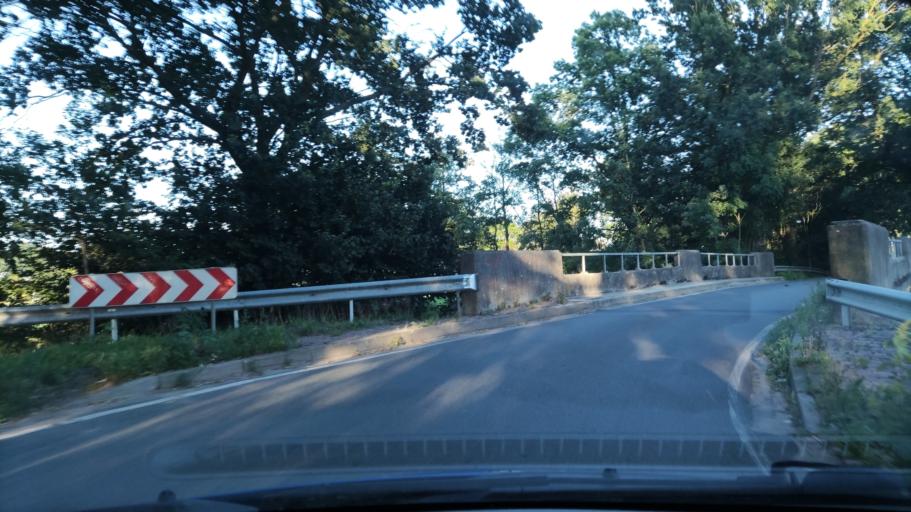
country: DE
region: Lower Saxony
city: Jameln
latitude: 53.0443
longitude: 11.1158
